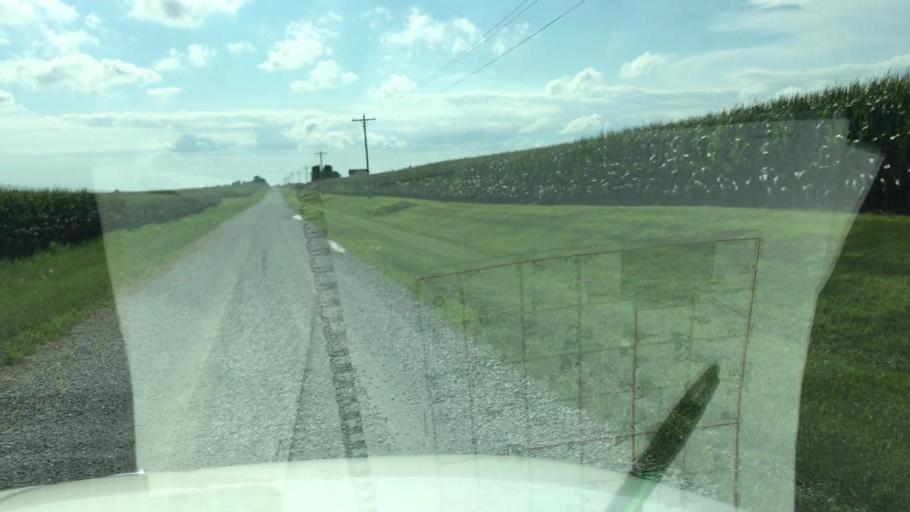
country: US
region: Illinois
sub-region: Hancock County
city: Nauvoo
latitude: 40.5212
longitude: -91.2721
